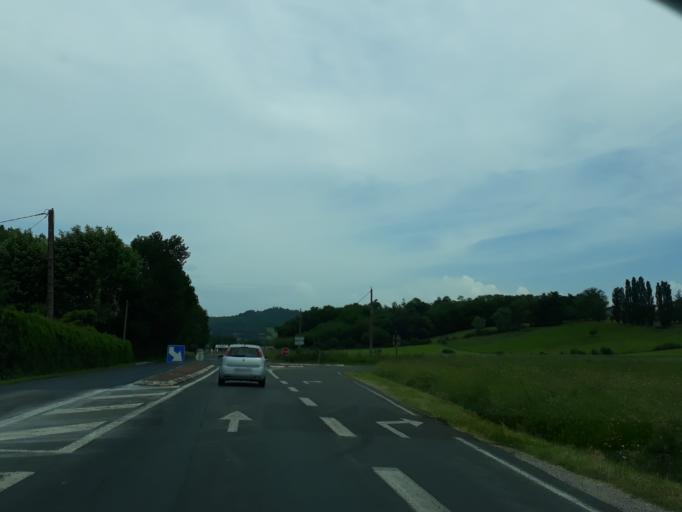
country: FR
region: Limousin
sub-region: Departement de la Correze
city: Larche
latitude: 45.1253
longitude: 1.3968
